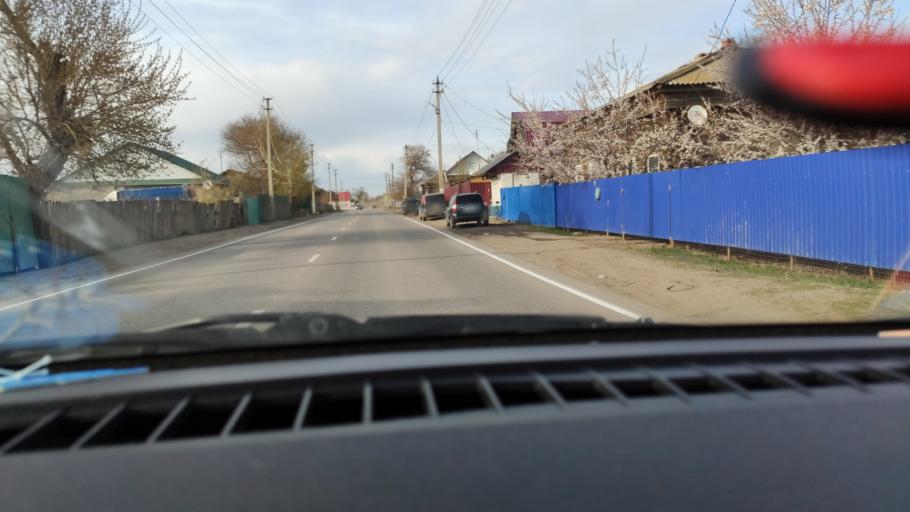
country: RU
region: Saratov
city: Privolzhskiy
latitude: 51.2059
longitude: 45.9179
